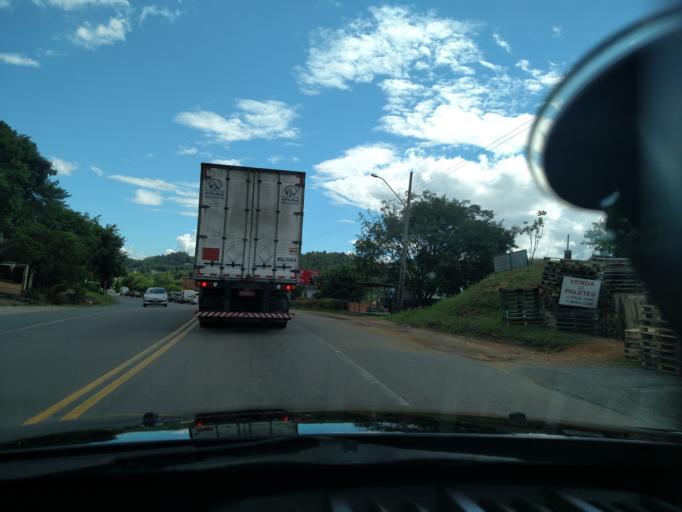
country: BR
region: Santa Catarina
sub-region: Blumenau
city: Blumenau
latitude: -26.8712
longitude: -49.1112
